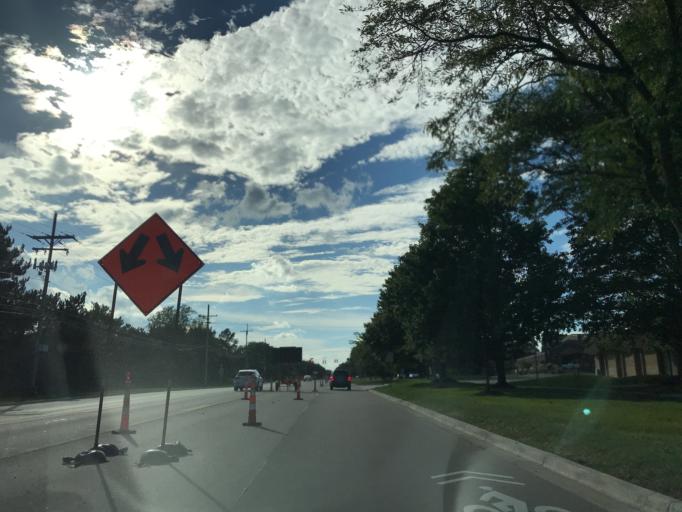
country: US
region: Michigan
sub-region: Oakland County
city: Farmington Hills
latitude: 42.5134
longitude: -83.3765
